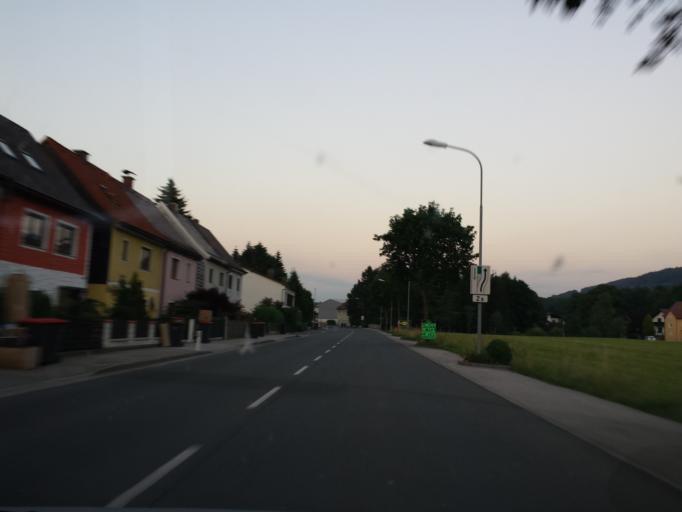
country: AT
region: Lower Austria
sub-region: Politischer Bezirk Lilienfeld
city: Hainfeld
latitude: 48.0337
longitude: 15.7807
